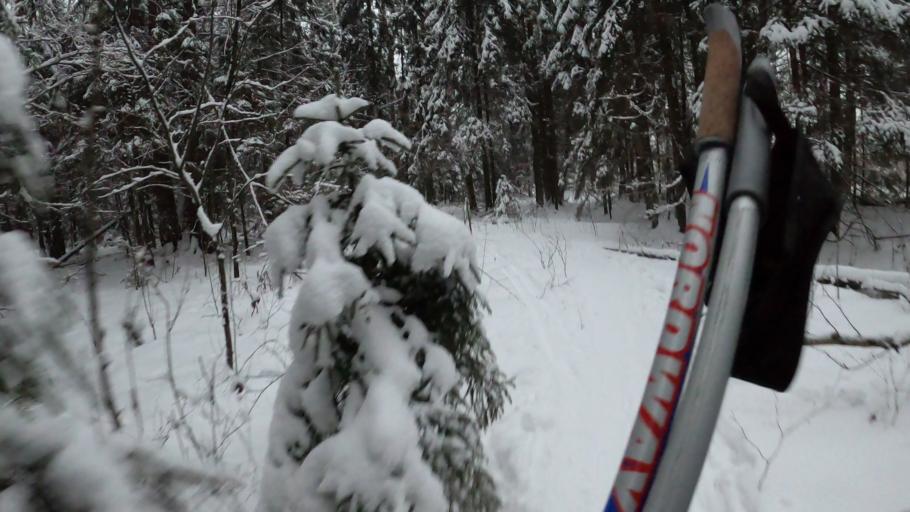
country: RU
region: Moskovskaya
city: Nakhabino
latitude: 55.8992
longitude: 37.2020
